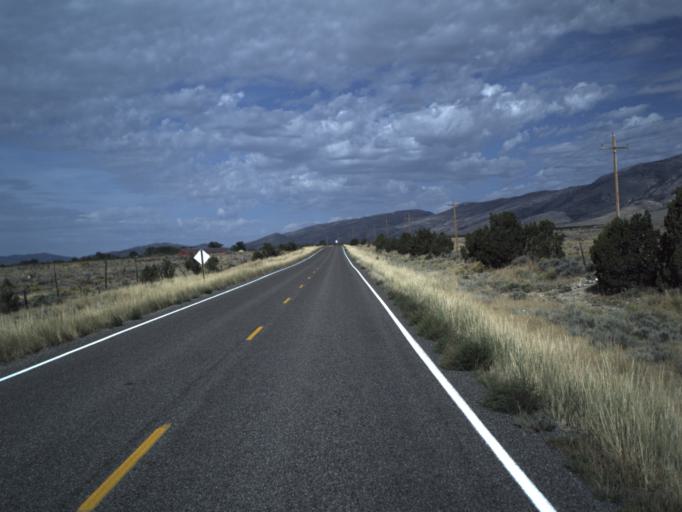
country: US
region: Idaho
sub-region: Cassia County
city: Burley
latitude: 41.8170
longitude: -113.3922
